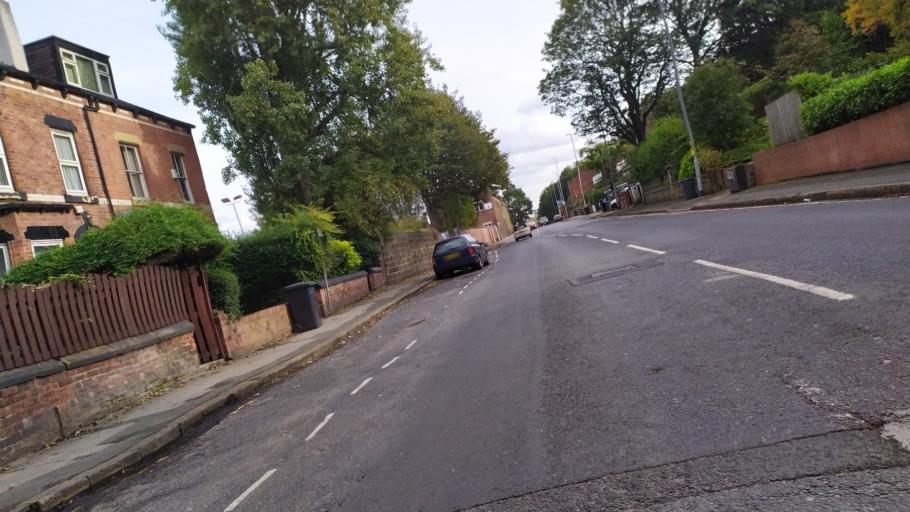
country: GB
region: England
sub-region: City and Borough of Leeds
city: Chapel Allerton
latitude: 53.8196
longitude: -1.5544
